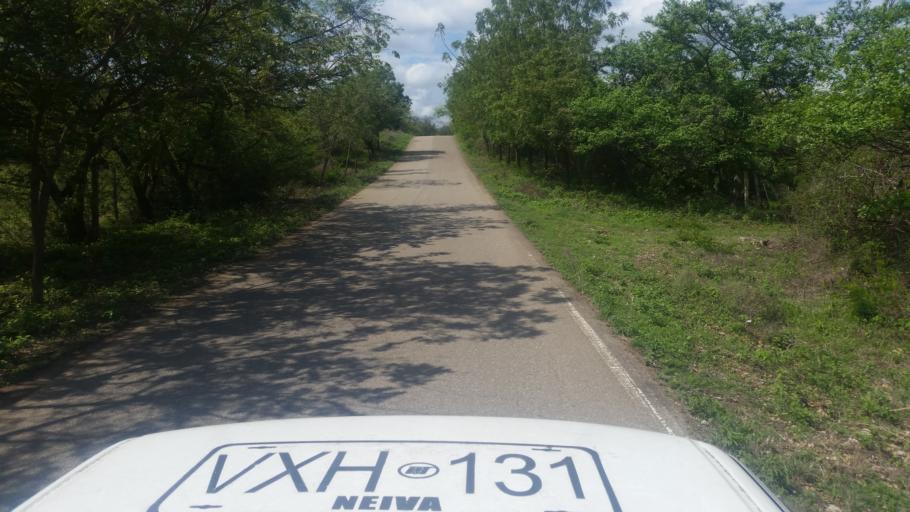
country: CO
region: Huila
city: Villavieja
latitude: 3.2005
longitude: -75.2102
